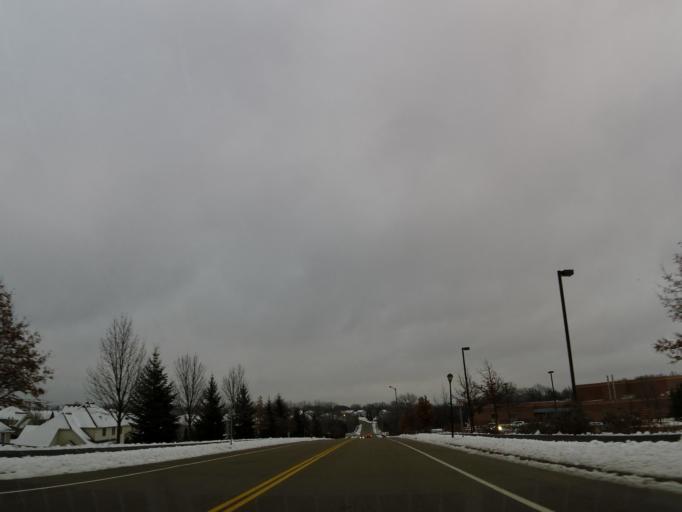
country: US
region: Minnesota
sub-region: Dakota County
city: Apple Valley
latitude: 44.7102
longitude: -93.2427
